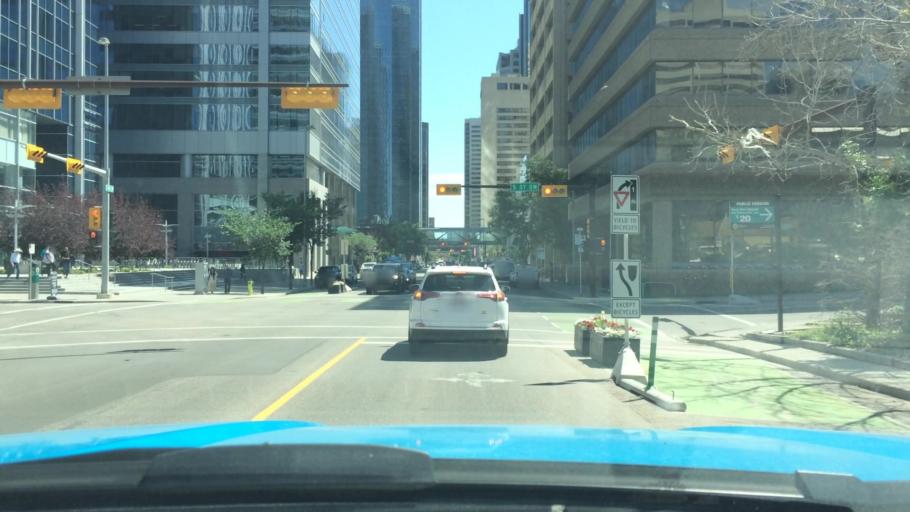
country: CA
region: Alberta
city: Calgary
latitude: 51.0505
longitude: -114.0741
